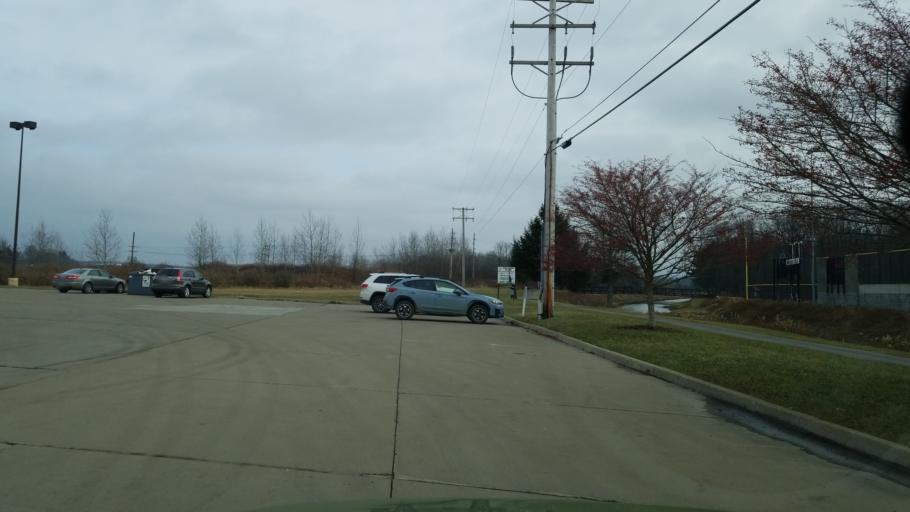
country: US
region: Pennsylvania
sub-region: Clearfield County
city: DuBois
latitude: 41.1186
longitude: -78.7556
